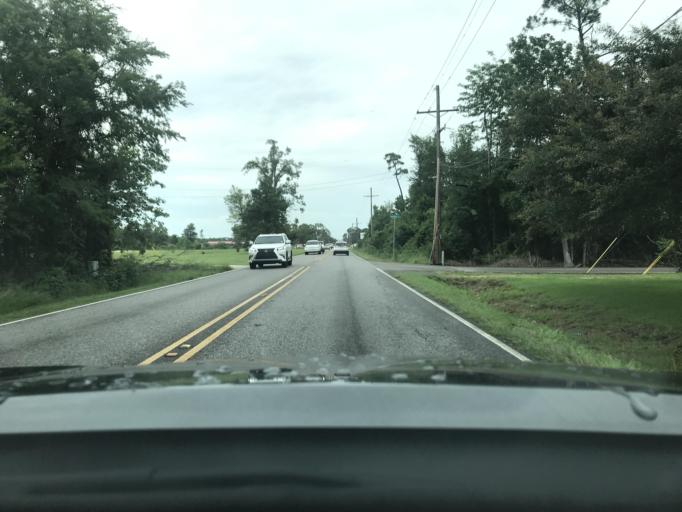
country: US
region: Louisiana
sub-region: Calcasieu Parish
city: Westlake
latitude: 30.2712
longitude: -93.2582
